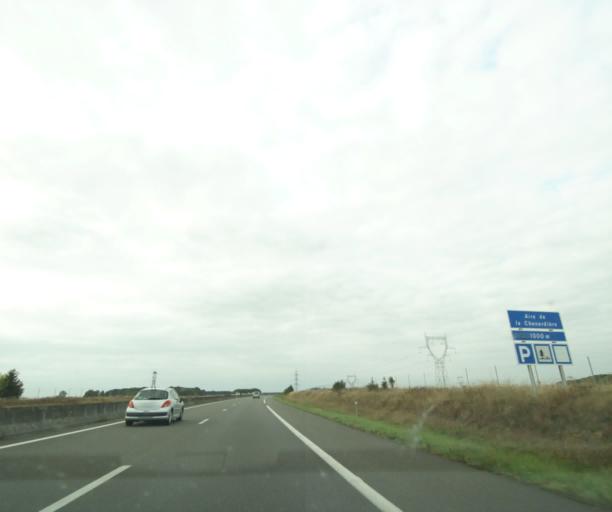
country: FR
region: Centre
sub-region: Departement d'Indre-et-Loire
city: Rouziers-de-Touraine
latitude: 47.5246
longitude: 0.6233
